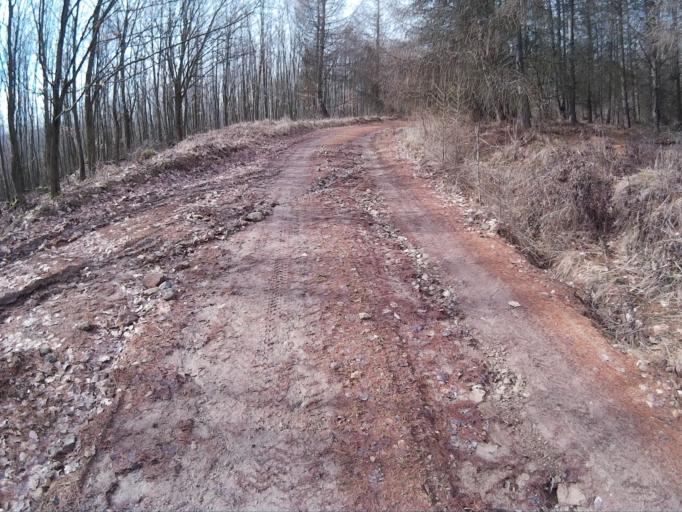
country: HU
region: Borsod-Abauj-Zemplen
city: Tolcsva
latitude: 48.4075
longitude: 21.4466
